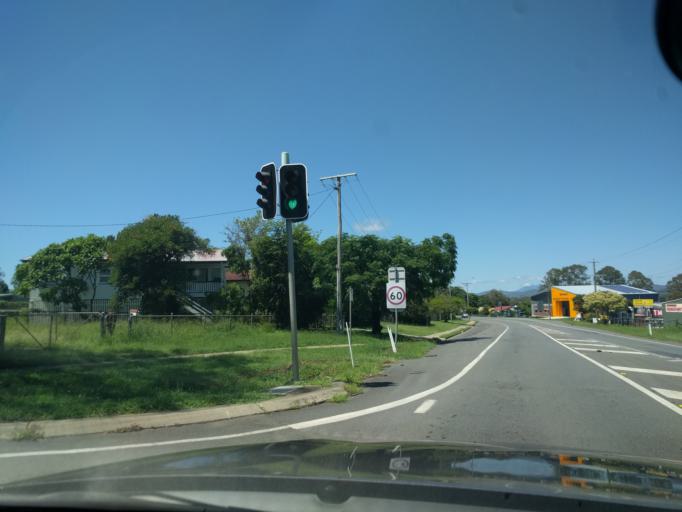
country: AU
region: Queensland
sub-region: Logan
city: Cedar Vale
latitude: -27.9725
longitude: 152.9959
